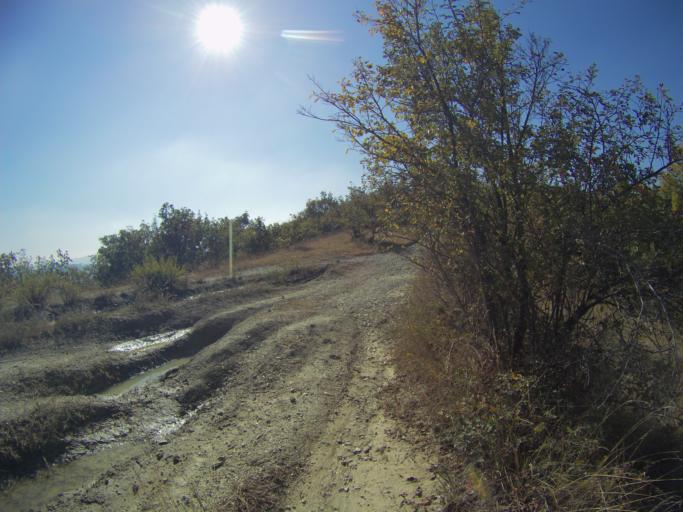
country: IT
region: Emilia-Romagna
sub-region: Provincia di Reggio Emilia
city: Quattro Castella
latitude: 44.5892
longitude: 10.4877
